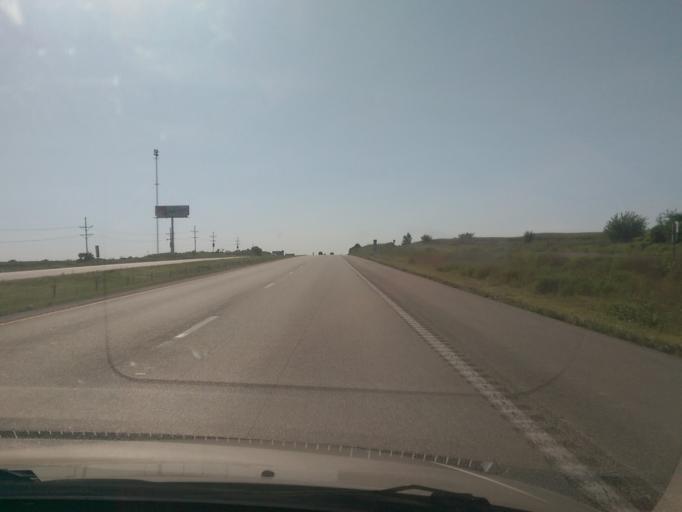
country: US
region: Missouri
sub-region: Saline County
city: Sweet Springs
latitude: 38.9809
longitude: -93.4753
